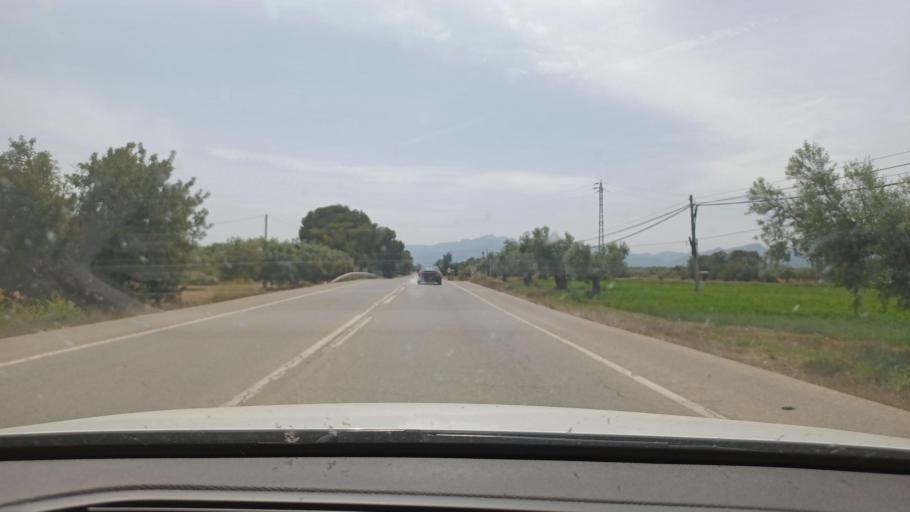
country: ES
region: Catalonia
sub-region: Provincia de Tarragona
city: Cambrils
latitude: 41.0457
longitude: 0.9903
